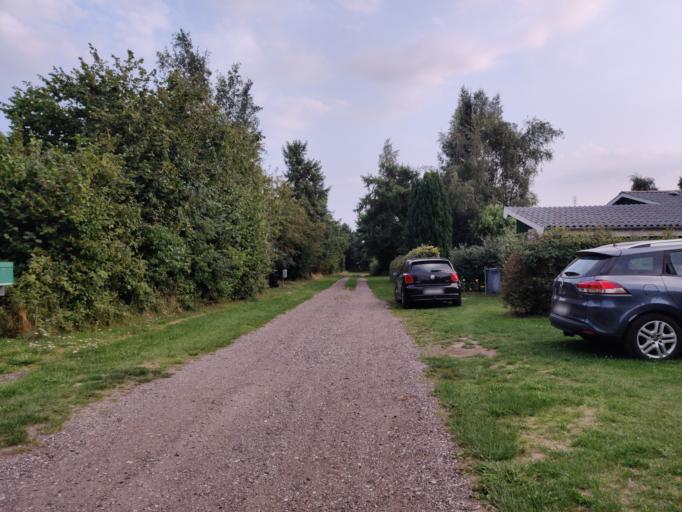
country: DK
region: Zealand
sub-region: Guldborgsund Kommune
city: Nykobing Falster
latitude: 54.5964
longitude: 11.9658
